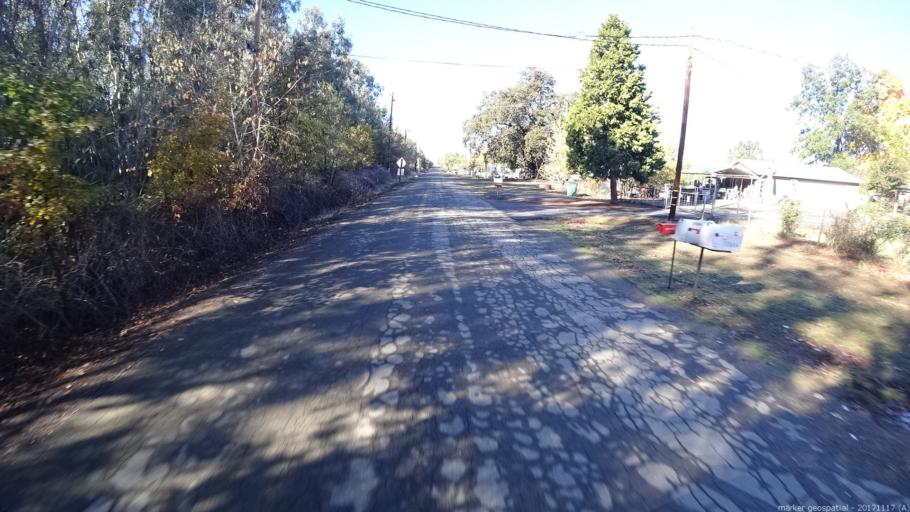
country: US
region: California
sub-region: Shasta County
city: Anderson
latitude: 40.4341
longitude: -122.2565
